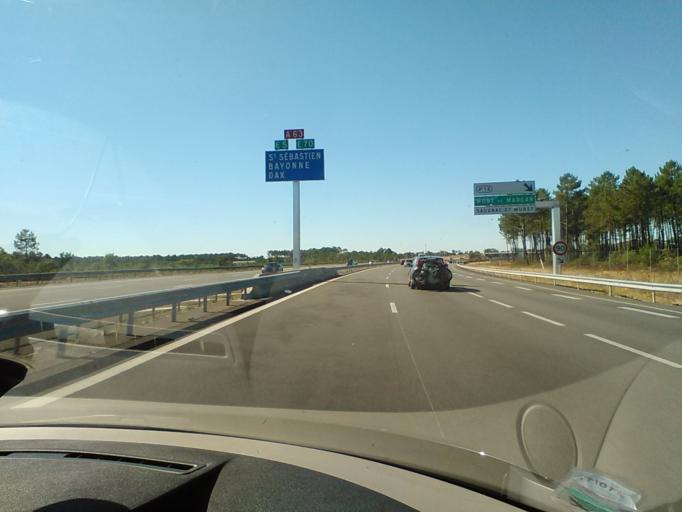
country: FR
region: Aquitaine
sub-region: Departement de la Gironde
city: Belin-Beliet
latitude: 44.4059
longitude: -0.8184
